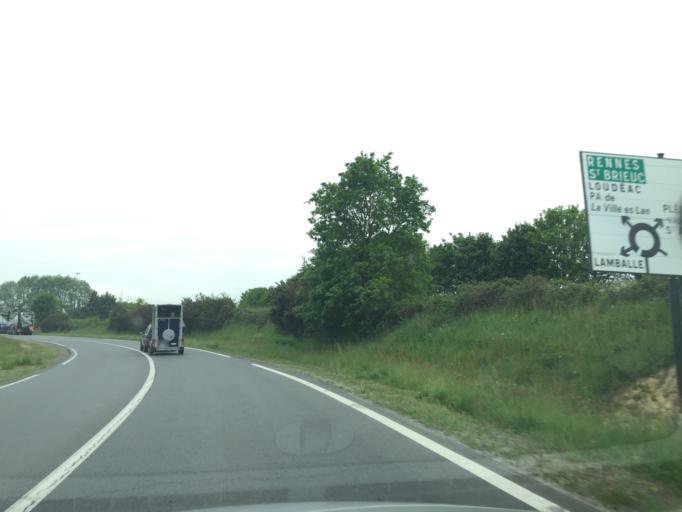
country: FR
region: Brittany
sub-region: Departement des Cotes-d'Armor
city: Lamballe
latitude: 48.4820
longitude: -2.5105
